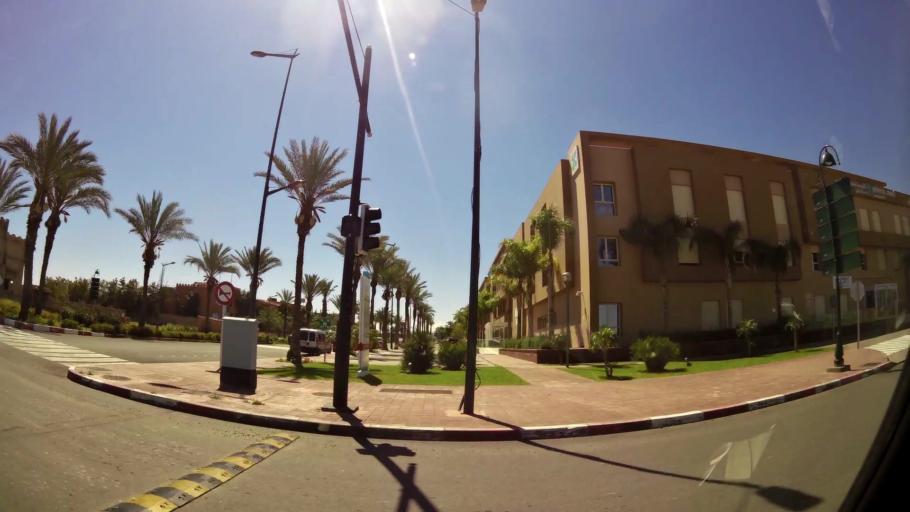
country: MA
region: Marrakech-Tensift-Al Haouz
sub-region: Marrakech
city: Marrakesh
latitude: 31.5907
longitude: -8.0022
